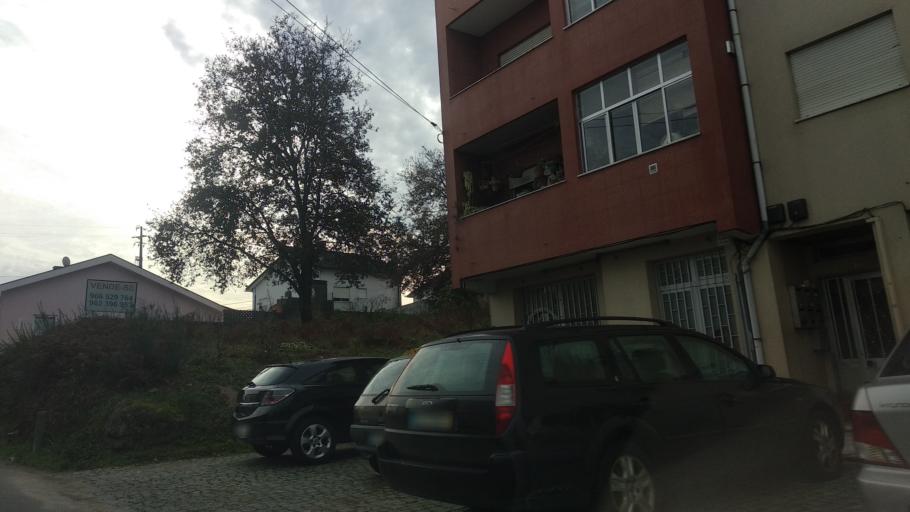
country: PT
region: Braga
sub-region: Braga
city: Braga
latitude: 41.5268
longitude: -8.4404
